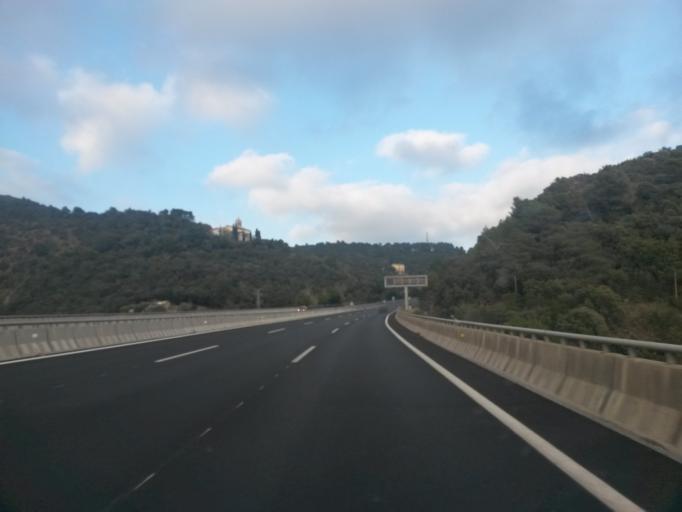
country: ES
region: Catalonia
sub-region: Provincia de Barcelona
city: Pineda de Mar
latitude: 41.6435
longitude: 2.6771
